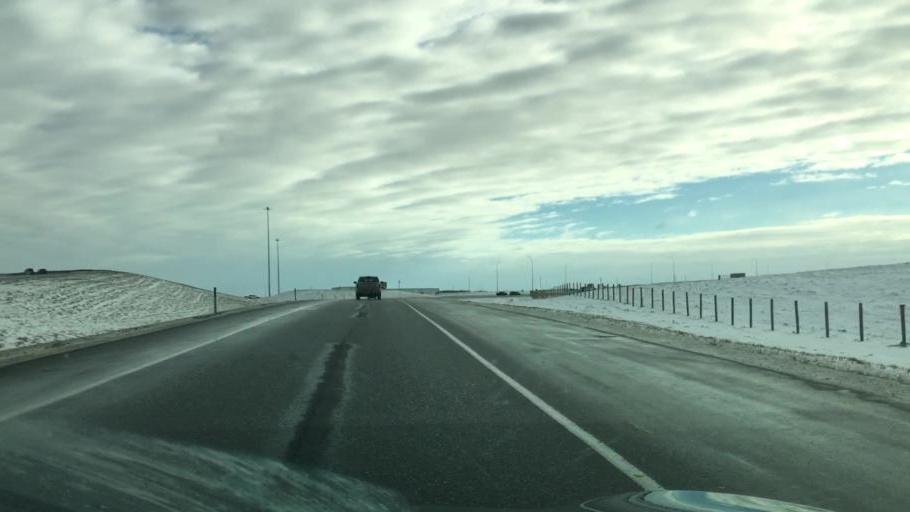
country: CA
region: Alberta
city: Airdrie
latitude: 51.1740
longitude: -114.0054
